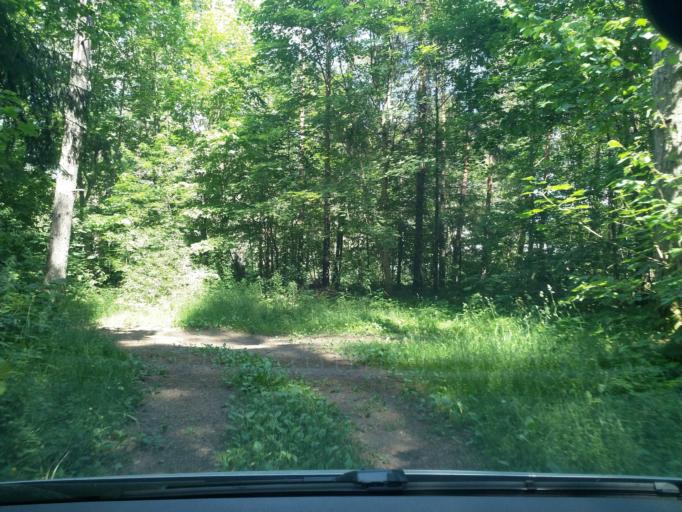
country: LV
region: Kuldigas Rajons
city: Kuldiga
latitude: 56.9700
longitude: 21.9240
